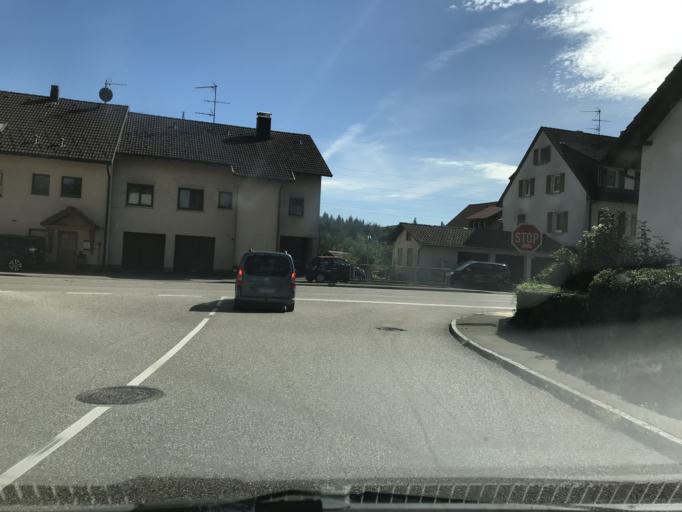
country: DE
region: Baden-Wuerttemberg
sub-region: Freiburg Region
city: Schworstadt
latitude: 47.5910
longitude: 7.8663
